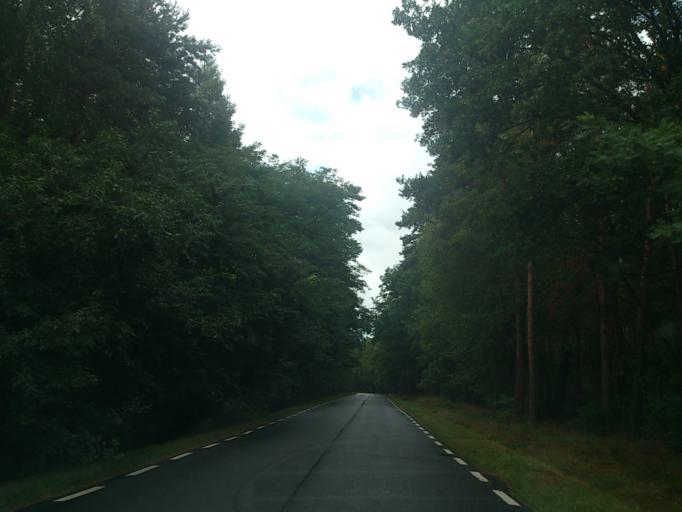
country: PL
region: Greater Poland Voivodeship
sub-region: Powiat poznanski
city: Pobiedziska
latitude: 52.5121
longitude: 17.2001
